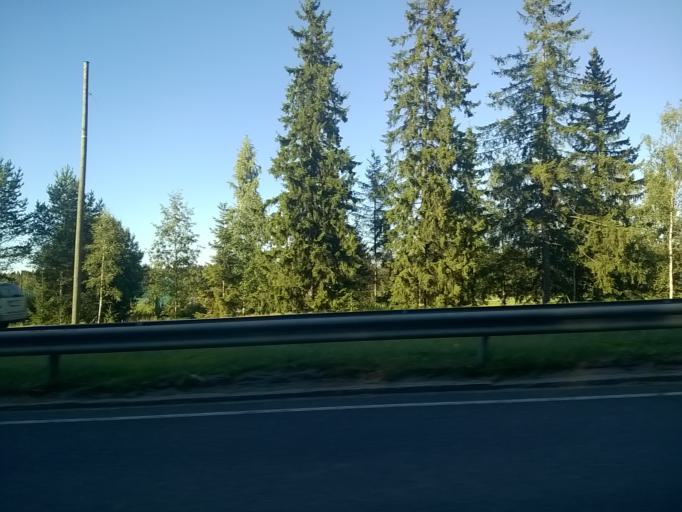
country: FI
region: Pirkanmaa
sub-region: Tampere
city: Tampere
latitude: 61.5044
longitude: 23.8517
